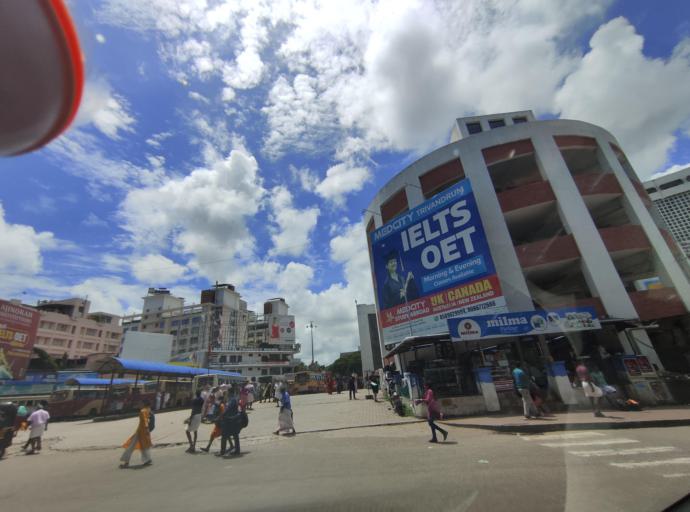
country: IN
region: Kerala
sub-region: Thiruvananthapuram
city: Thiruvananthapuram
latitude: 8.4881
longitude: 76.9514
